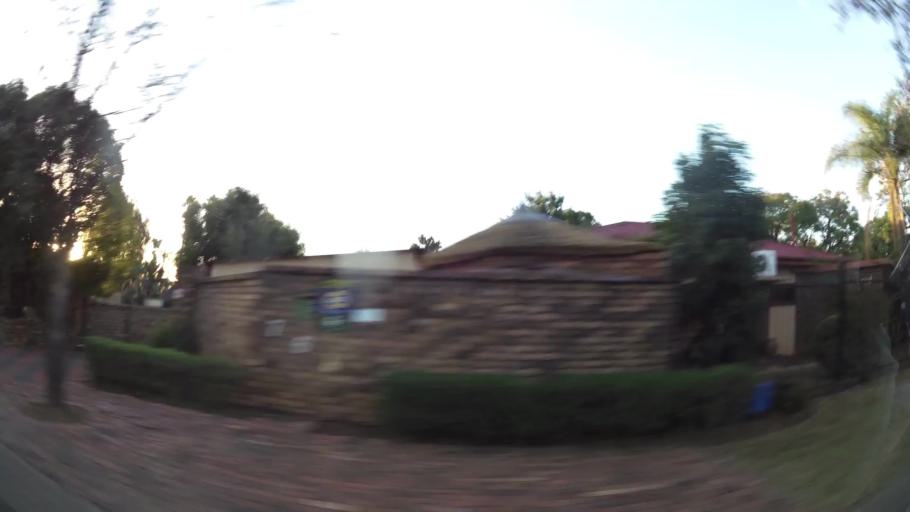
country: ZA
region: Gauteng
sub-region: City of Tshwane Metropolitan Municipality
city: Pretoria
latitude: -25.7121
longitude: 28.2188
